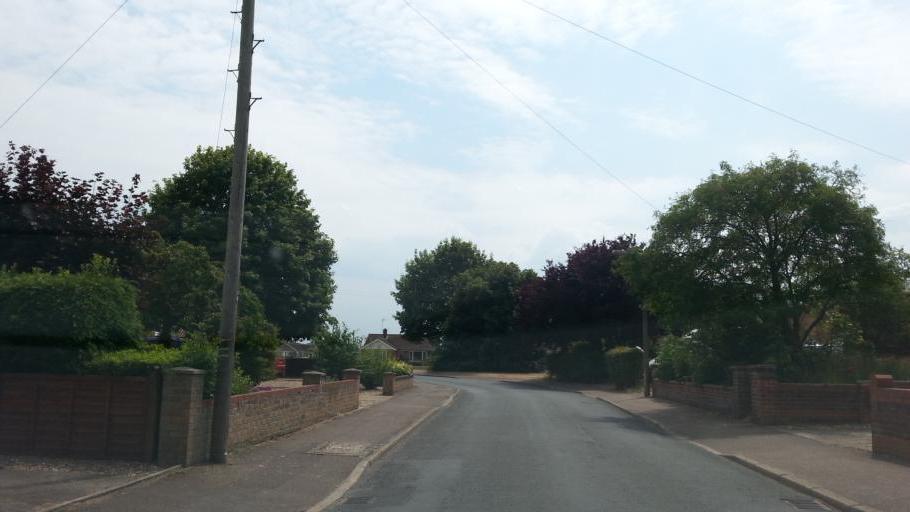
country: GB
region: England
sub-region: Suffolk
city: Lakenheath
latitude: 52.4167
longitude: 0.5286
